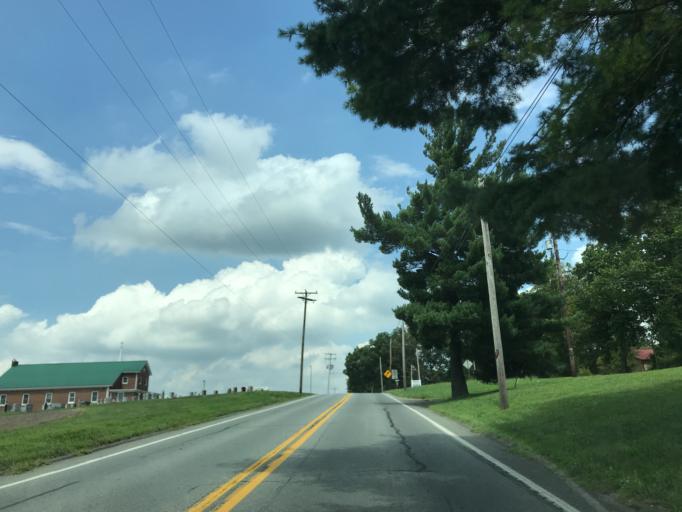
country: US
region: Pennsylvania
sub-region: York County
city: Red Lion
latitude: 39.8640
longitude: -76.6198
